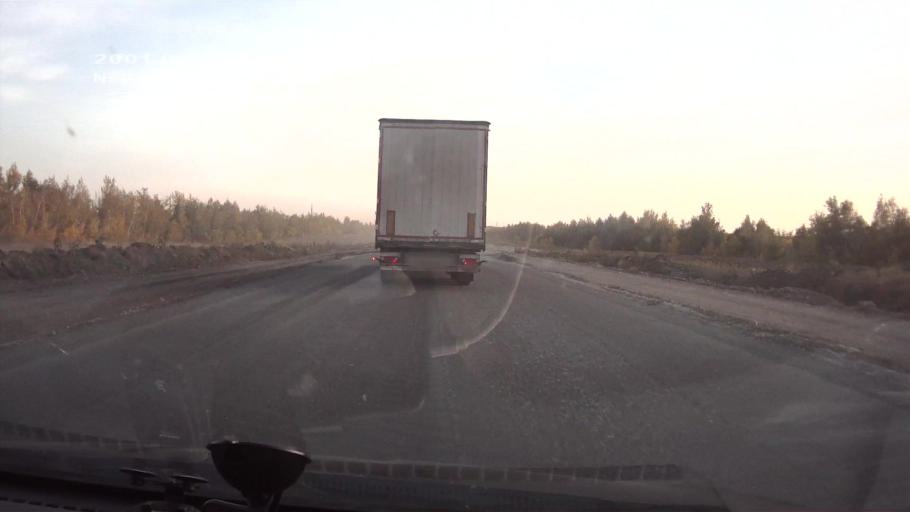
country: RU
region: Saratov
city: Kamenskiy
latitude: 50.9279
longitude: 45.5994
